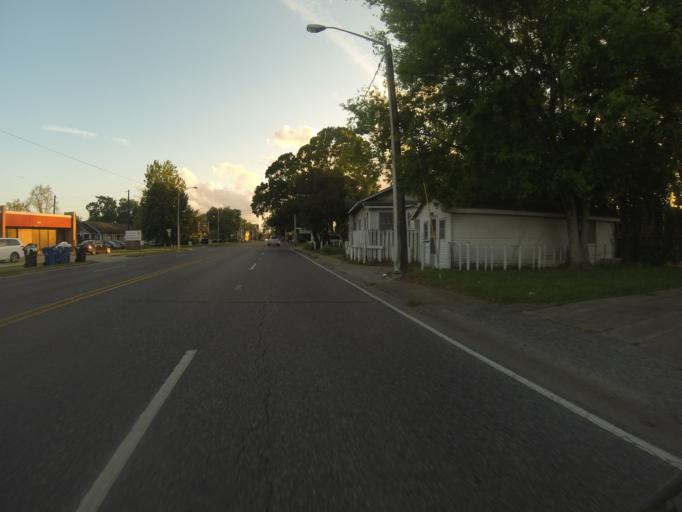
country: US
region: Louisiana
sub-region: Lafayette Parish
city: Lafayette
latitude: 30.2244
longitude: -92.0147
